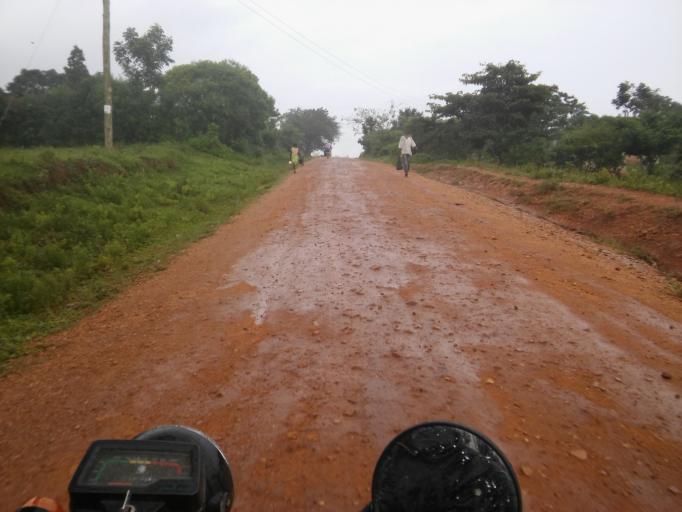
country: UG
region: Eastern Region
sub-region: Mbale District
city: Mbale
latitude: 0.9829
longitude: 34.2019
